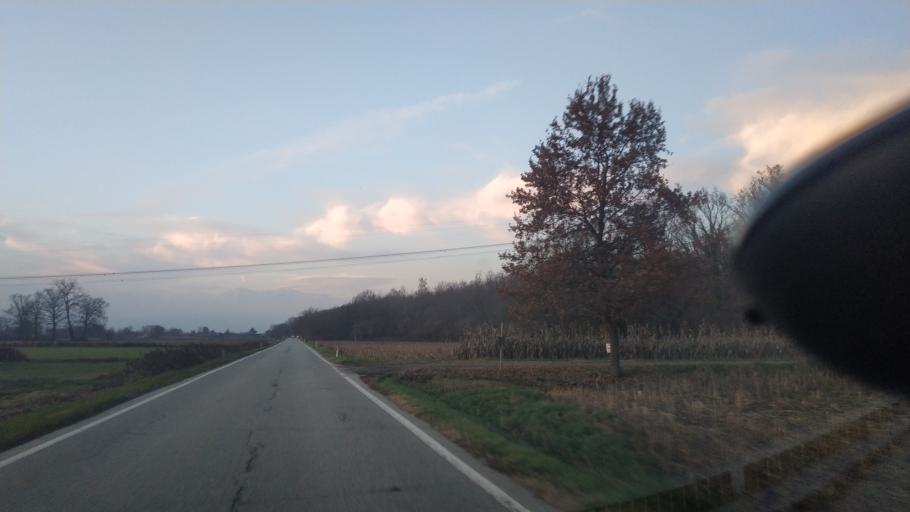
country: IT
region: Piedmont
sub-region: Provincia di Torino
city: Foglizzo
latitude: 45.2584
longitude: 7.8323
